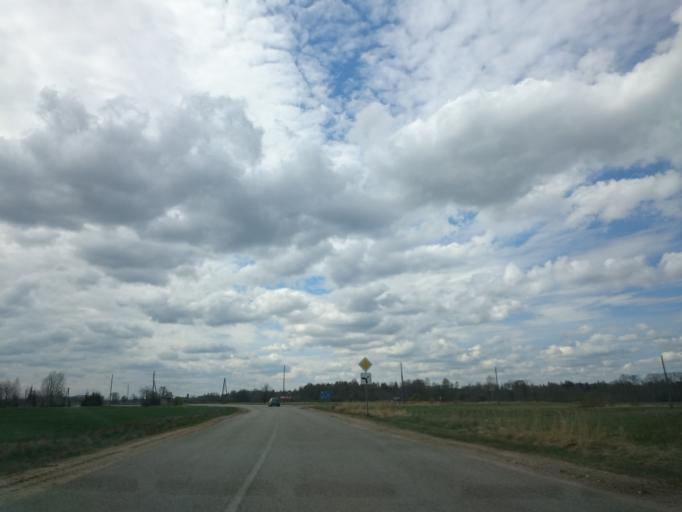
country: LV
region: Talsu Rajons
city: Sabile
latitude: 56.9606
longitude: 22.6177
